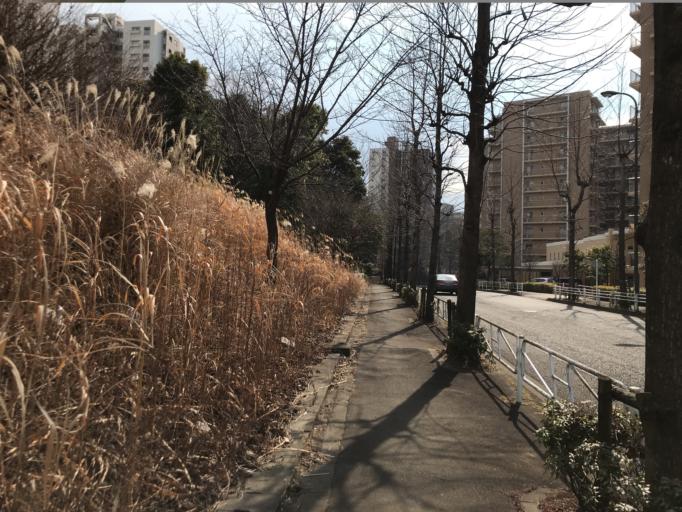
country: JP
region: Tokyo
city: Hino
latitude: 35.6216
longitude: 139.3783
